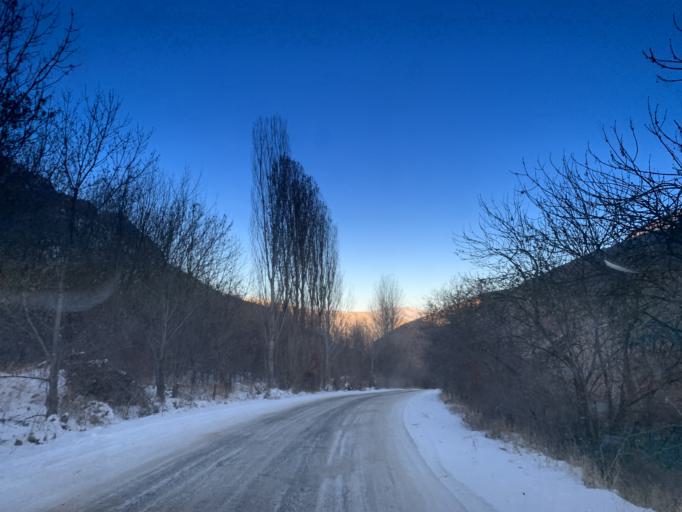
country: AM
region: Vayots' Dzori Marz
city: Areni
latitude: 39.6826
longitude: 45.2310
